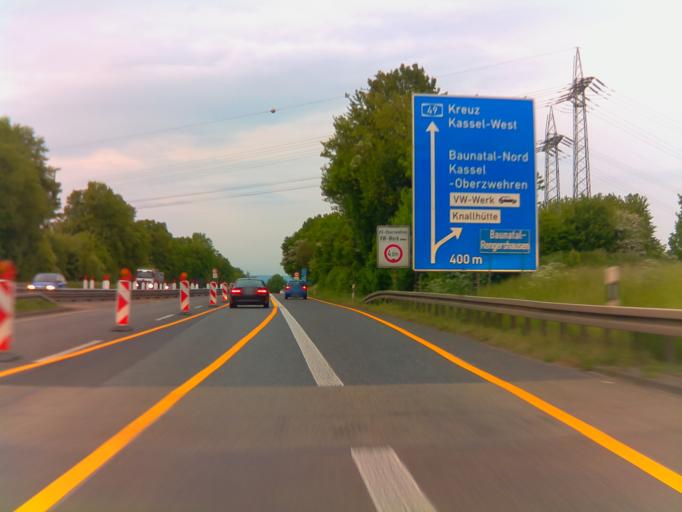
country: DE
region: Hesse
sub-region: Regierungsbezirk Kassel
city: Baunatal
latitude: 51.2513
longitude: 9.4399
